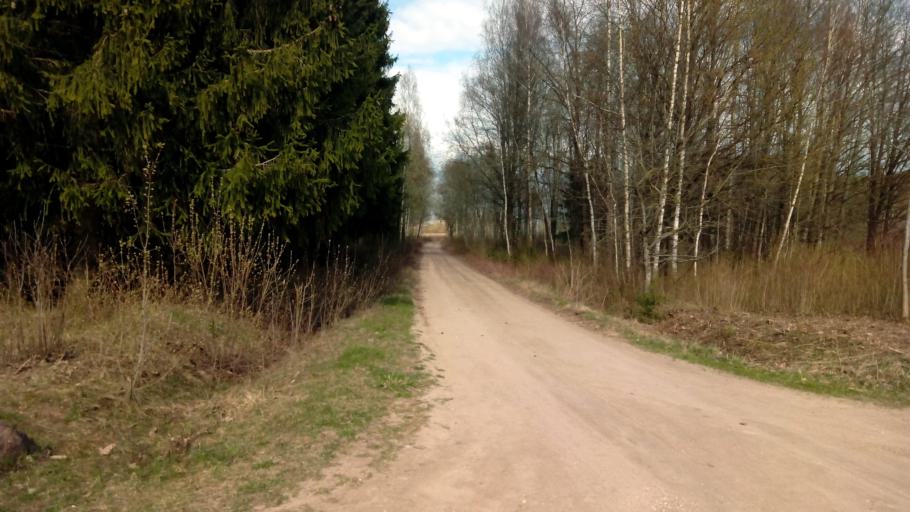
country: LT
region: Siauliu apskritis
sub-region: Siauliai
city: Siauliai
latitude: 55.9315
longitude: 23.3461
